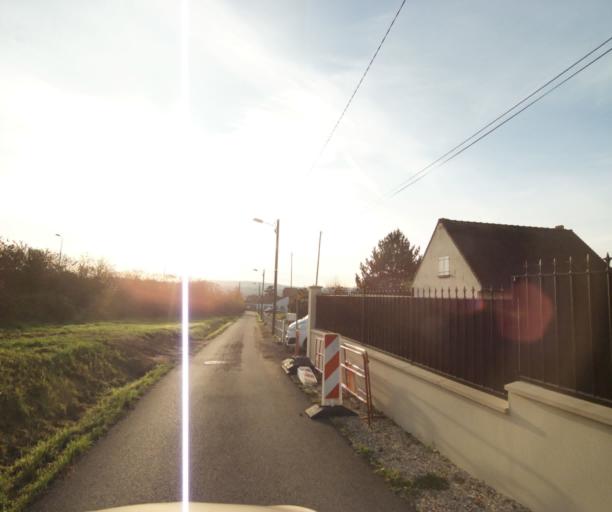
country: FR
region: Ile-de-France
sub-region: Departement des Yvelines
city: Triel-sur-Seine
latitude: 48.9701
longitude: 2.0135
